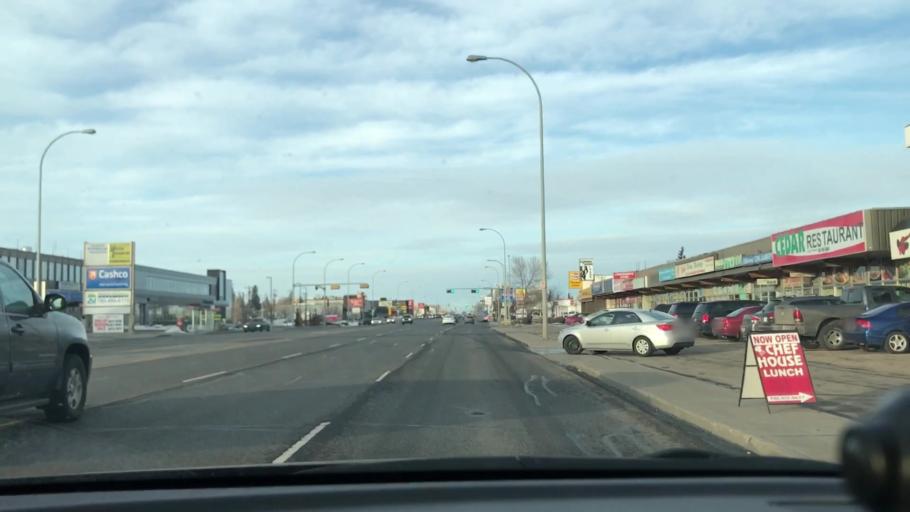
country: CA
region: Alberta
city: Edmonton
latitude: 53.5878
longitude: -113.4919
